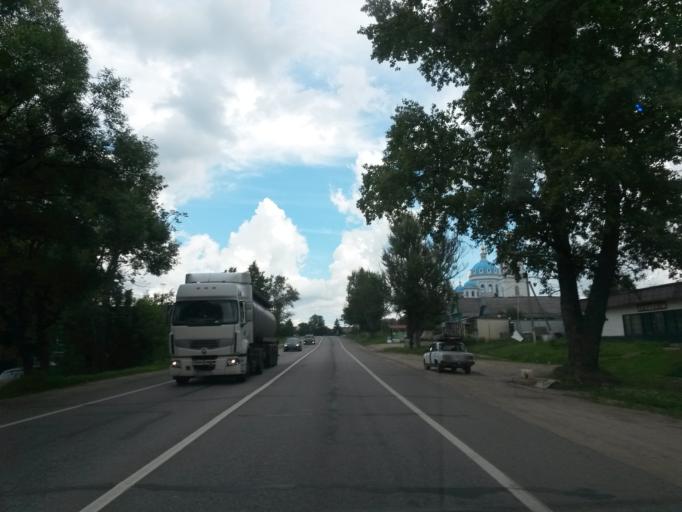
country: RU
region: Vladimir
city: Aleksandrov
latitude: 56.6004
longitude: 38.6270
